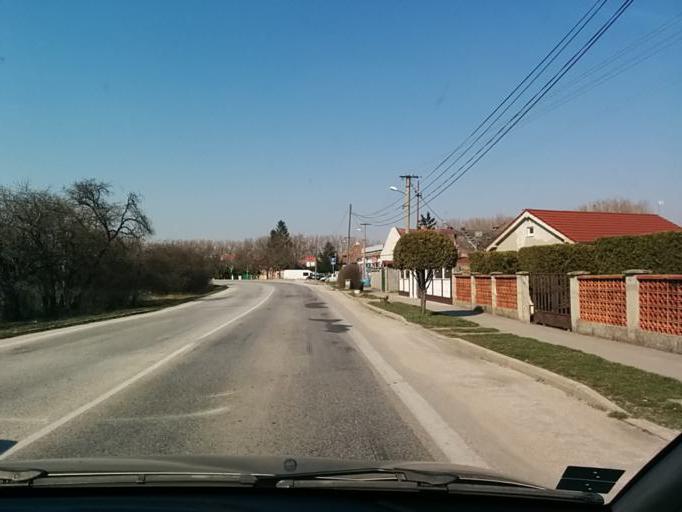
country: SK
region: Trnavsky
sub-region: Okres Galanta
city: Galanta
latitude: 48.2178
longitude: 17.7289
